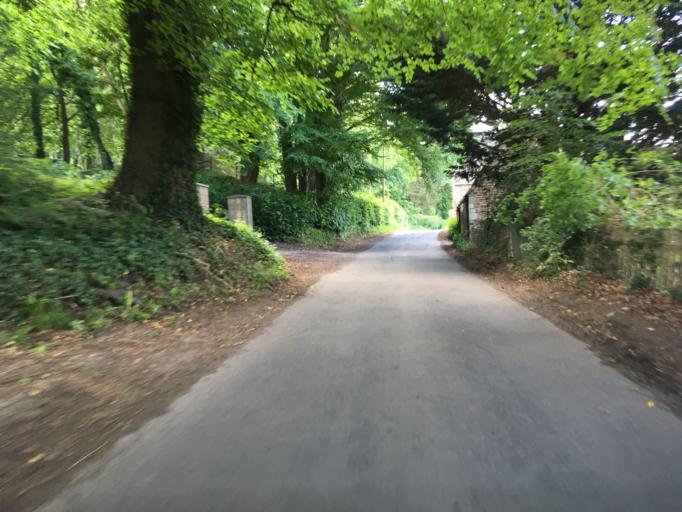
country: GB
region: England
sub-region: Gloucestershire
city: Stroud
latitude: 51.7677
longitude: -2.2018
